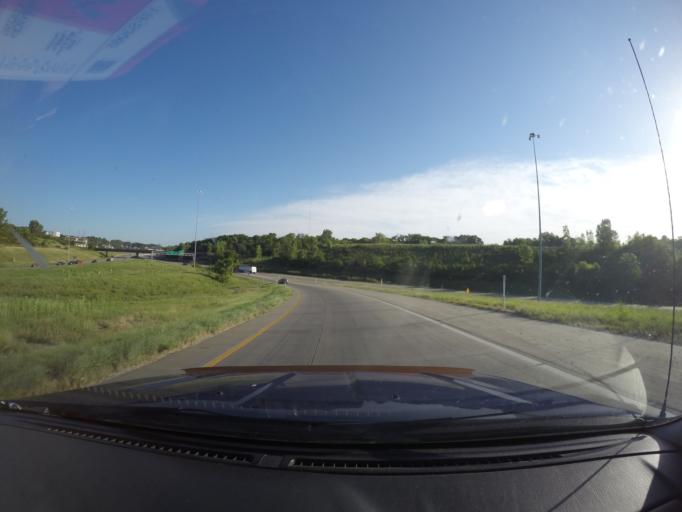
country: US
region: Kansas
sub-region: Wyandotte County
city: Kansas City
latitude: 39.1069
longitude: -94.6794
